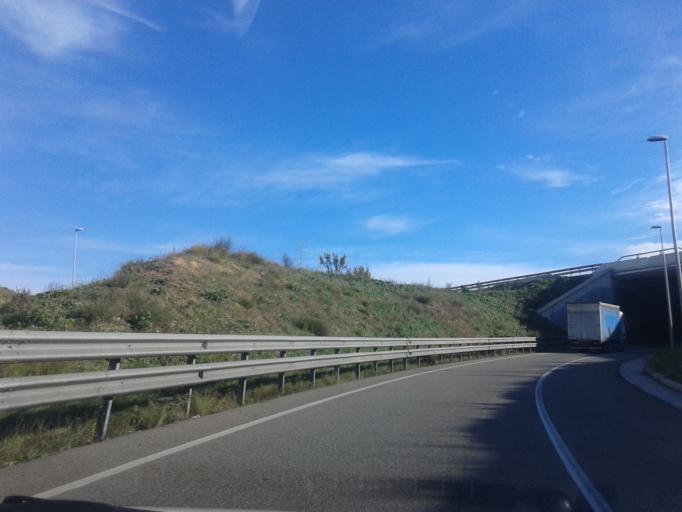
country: ES
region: Catalonia
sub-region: Provincia de Barcelona
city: Vilafranca del Penedes
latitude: 41.3521
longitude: 1.7186
